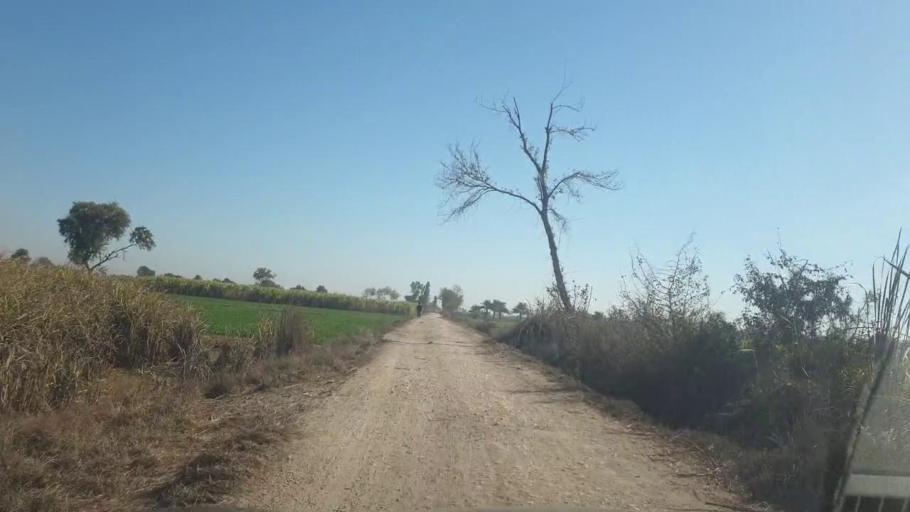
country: PK
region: Sindh
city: Ghotki
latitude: 27.9747
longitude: 69.3338
